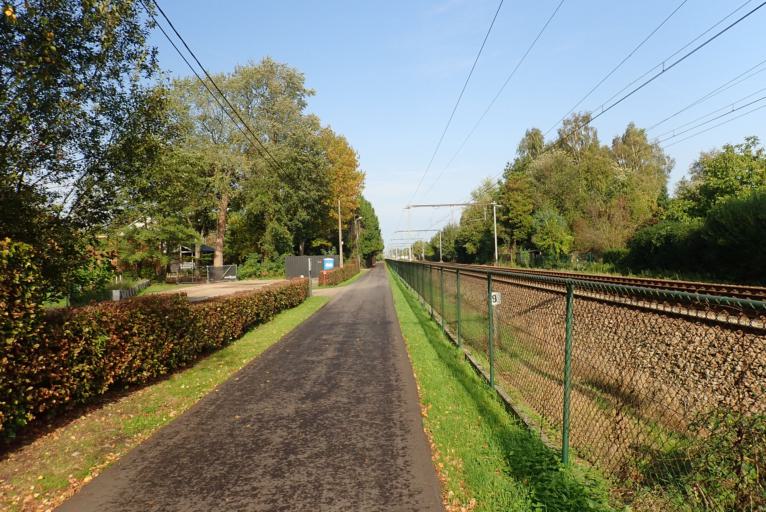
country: BE
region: Flanders
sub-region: Provincie Antwerpen
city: Kalmthout
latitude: 51.3953
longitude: 4.4663
